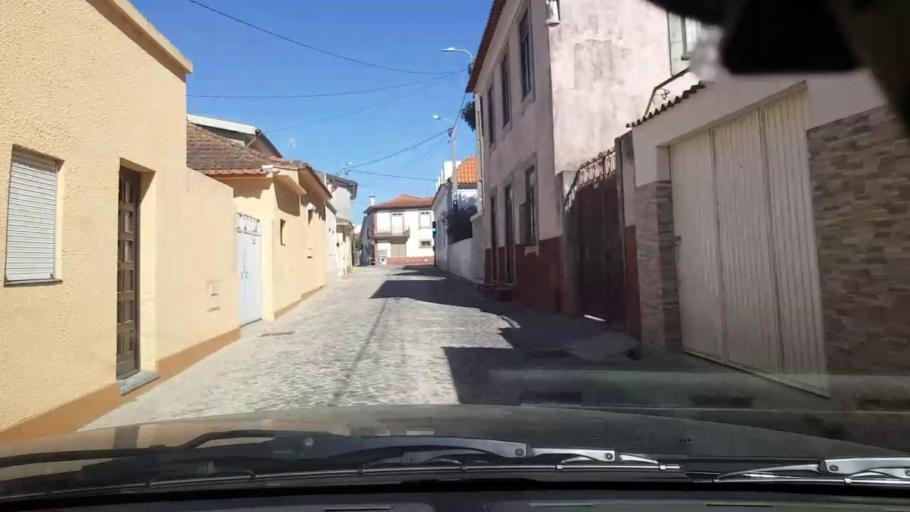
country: PT
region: Porto
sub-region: Maia
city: Gemunde
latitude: 41.2875
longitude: -8.6741
